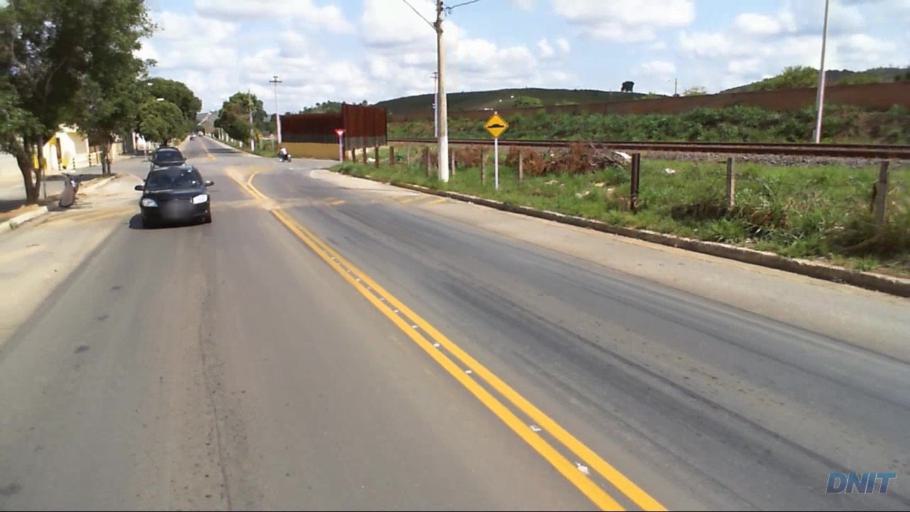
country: BR
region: Minas Gerais
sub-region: Governador Valadares
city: Governador Valadares
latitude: -18.9066
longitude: -41.9915
